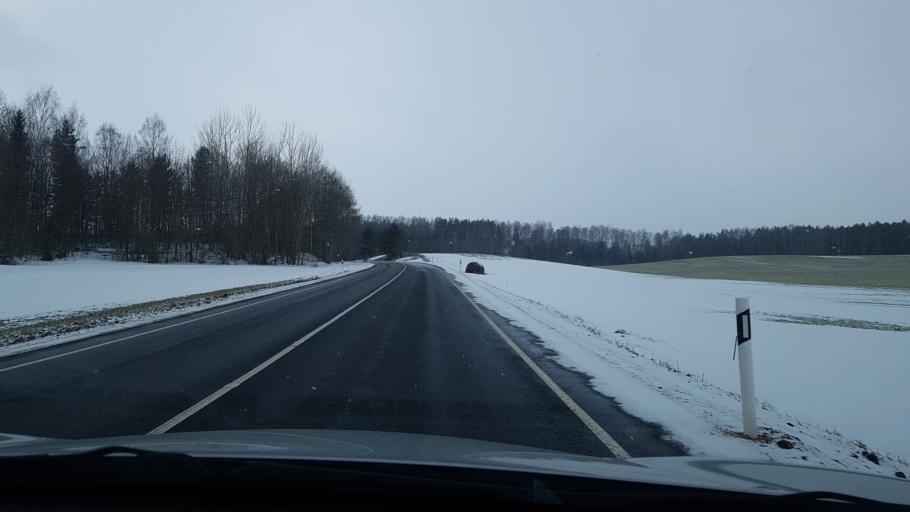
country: EE
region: Polvamaa
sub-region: Polva linn
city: Polva
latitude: 58.0917
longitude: 27.1354
